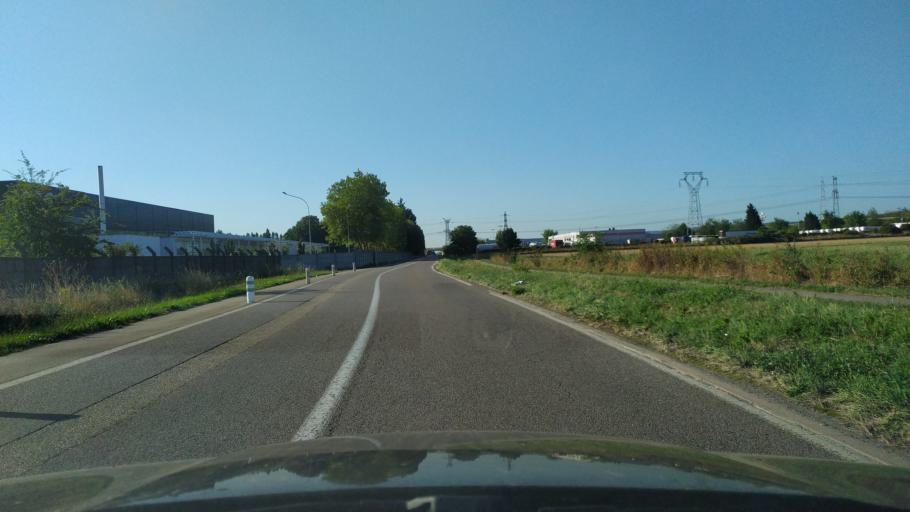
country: FR
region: Lorraine
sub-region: Departement de la Moselle
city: Maizieres-les-Metz
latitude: 49.2018
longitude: 6.1492
